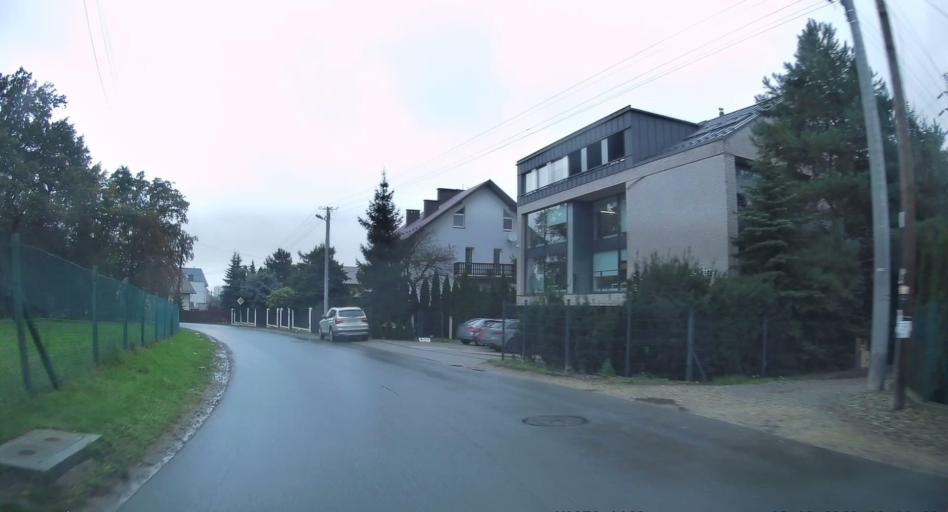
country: PL
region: Lesser Poland Voivodeship
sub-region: Powiat krakowski
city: Ochojno
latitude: 50.0074
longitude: 19.9831
